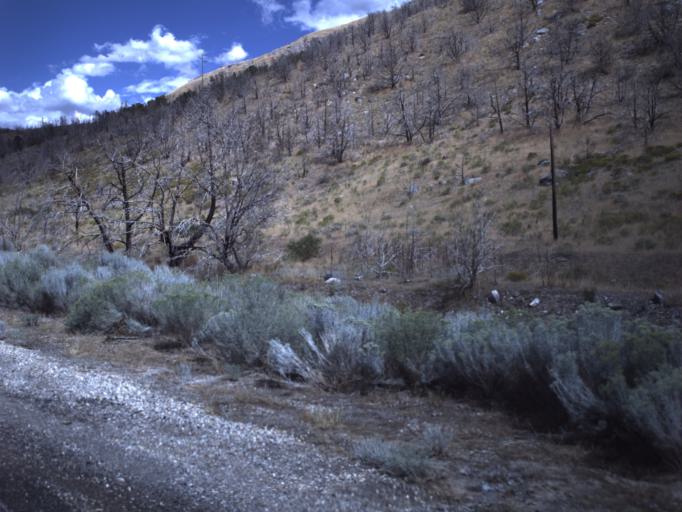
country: US
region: Utah
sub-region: Tooele County
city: Grantsville
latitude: 40.3416
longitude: -112.6069
